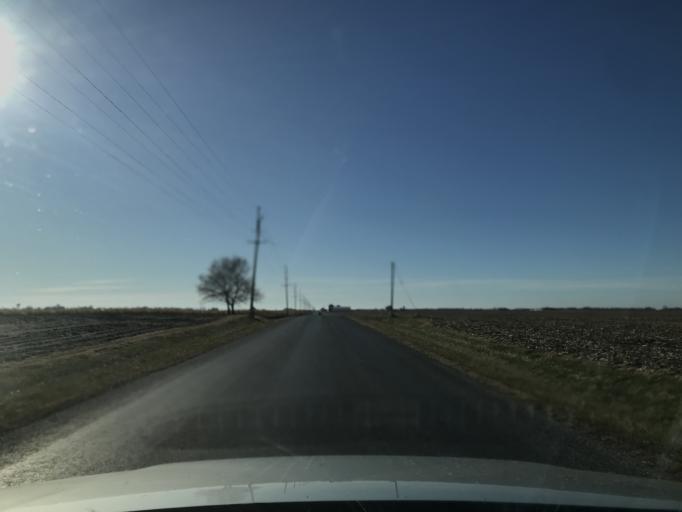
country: US
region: Illinois
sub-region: Hancock County
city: Carthage
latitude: 40.4842
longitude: -91.1781
